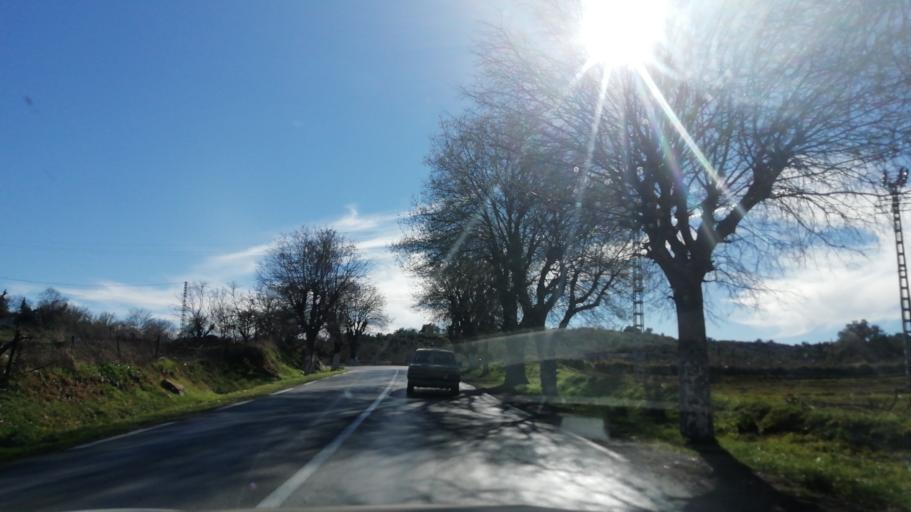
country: DZ
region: Tlemcen
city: Mansoura
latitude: 34.8353
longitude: -1.3727
